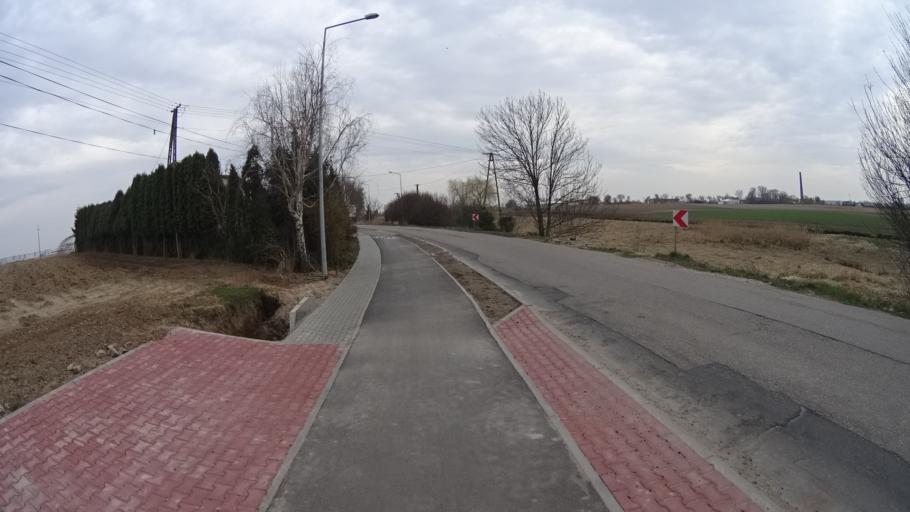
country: PL
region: Masovian Voivodeship
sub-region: Powiat warszawski zachodni
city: Blonie
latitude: 52.2129
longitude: 20.6530
